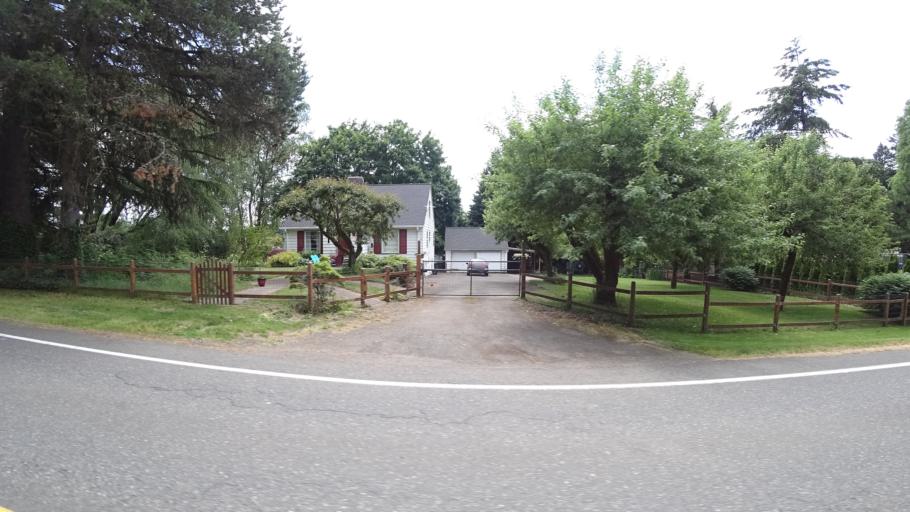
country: US
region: Oregon
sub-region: Clackamas County
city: Lake Oswego
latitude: 45.4401
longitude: -122.6996
